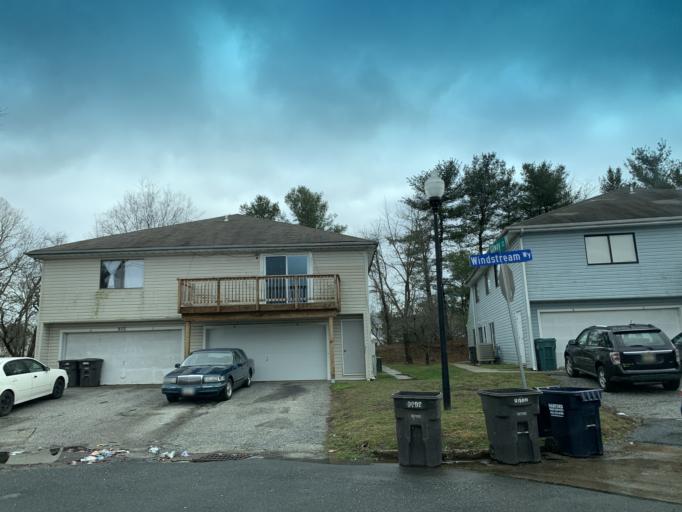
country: US
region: Maryland
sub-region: Harford County
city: Edgewood
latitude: 39.4270
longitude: -76.3197
